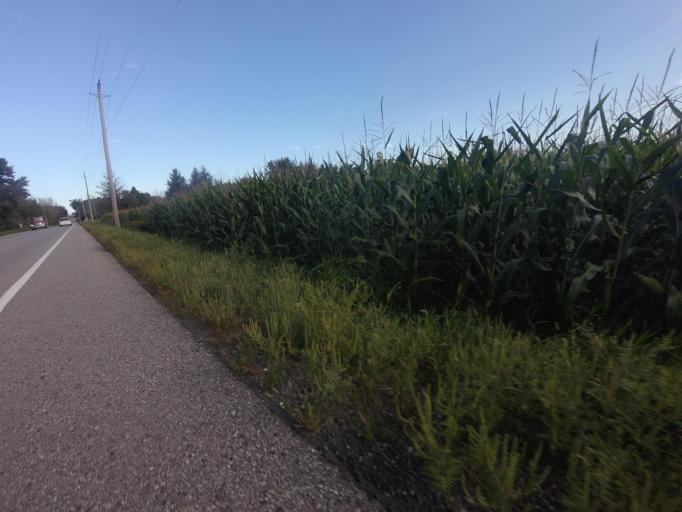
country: CA
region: Ontario
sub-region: Wellington County
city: Guelph
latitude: 43.5831
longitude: -80.3399
